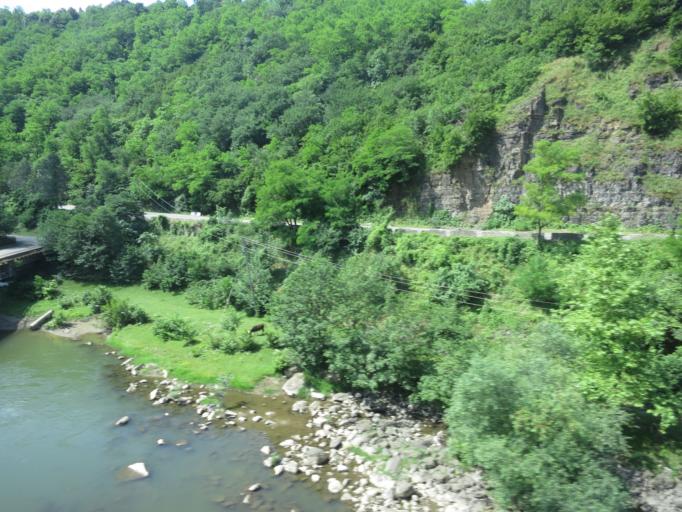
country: GE
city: Shorapani
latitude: 42.0940
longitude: 43.1290
